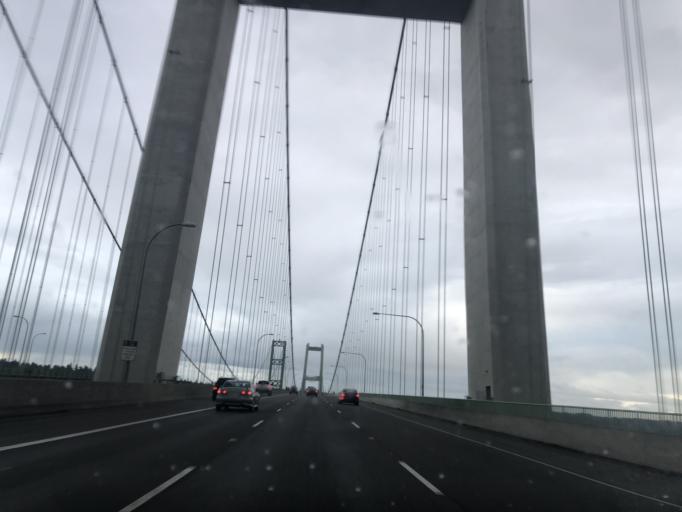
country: US
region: Washington
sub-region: Pierce County
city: Wollochet
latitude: 47.2713
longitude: -122.5551
